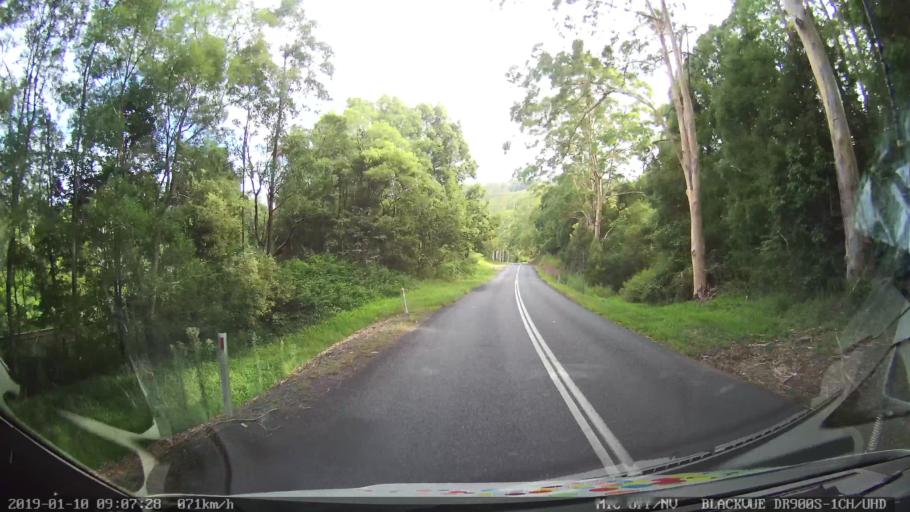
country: AU
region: New South Wales
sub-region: Coffs Harbour
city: Coffs Harbour
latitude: -30.2391
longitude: 153.0270
